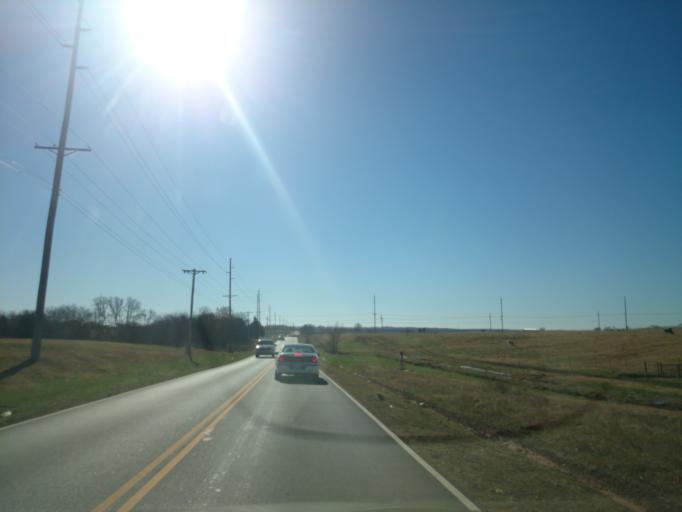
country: US
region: Oklahoma
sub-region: Payne County
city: Stillwater
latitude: 36.1331
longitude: -97.0873
